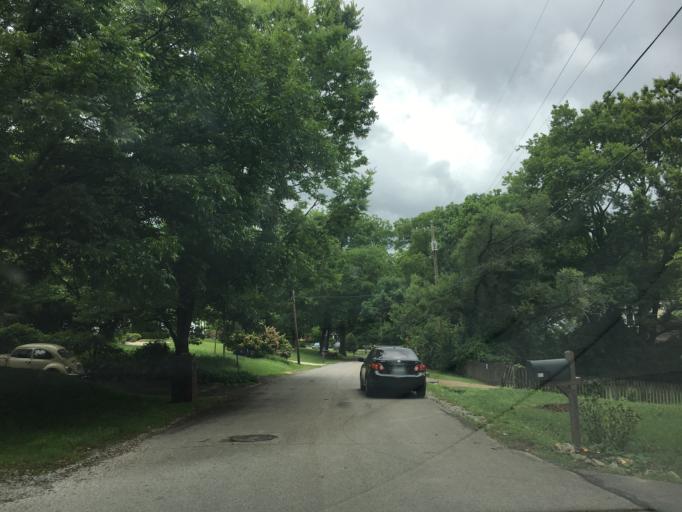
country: US
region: Tennessee
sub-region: Davidson County
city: Oak Hill
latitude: 36.1128
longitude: -86.7825
